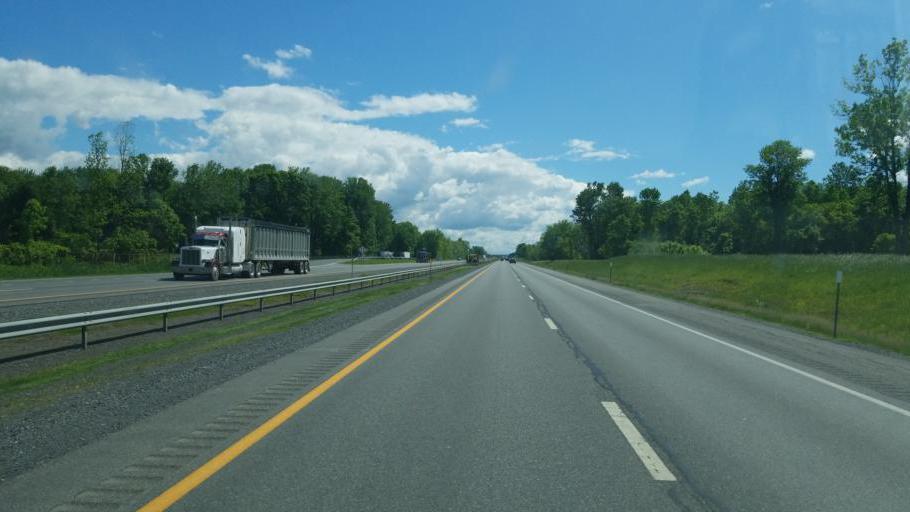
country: US
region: New York
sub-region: Madison County
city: Oneida
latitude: 43.1151
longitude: -75.6484
